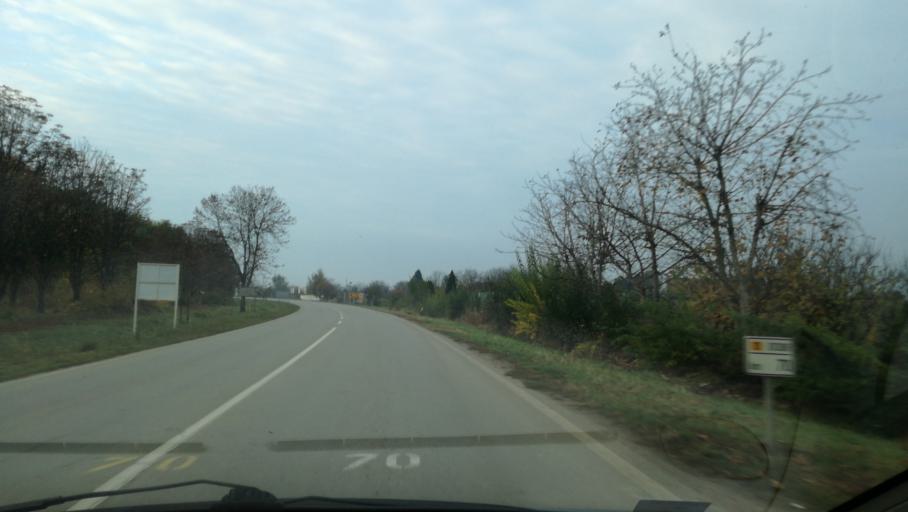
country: RS
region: Autonomna Pokrajina Vojvodina
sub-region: Severnobanatski Okrug
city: Kikinda
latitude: 45.8141
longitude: 20.4338
